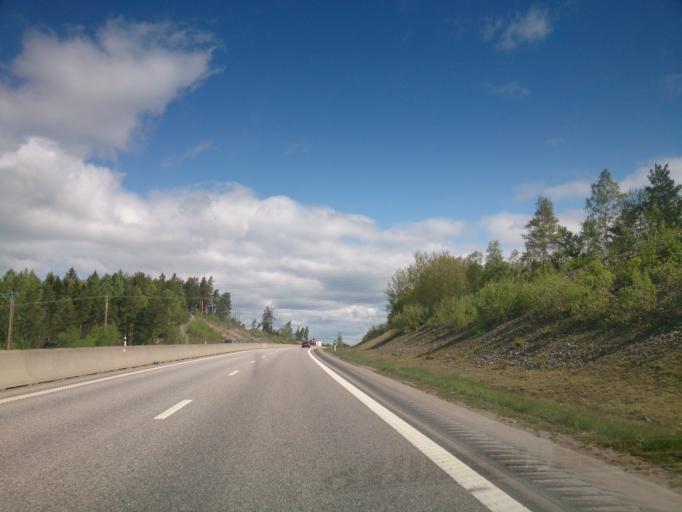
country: SE
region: OEstergoetland
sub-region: Norrkopings Kommun
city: Kimstad
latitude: 58.5126
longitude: 15.9938
